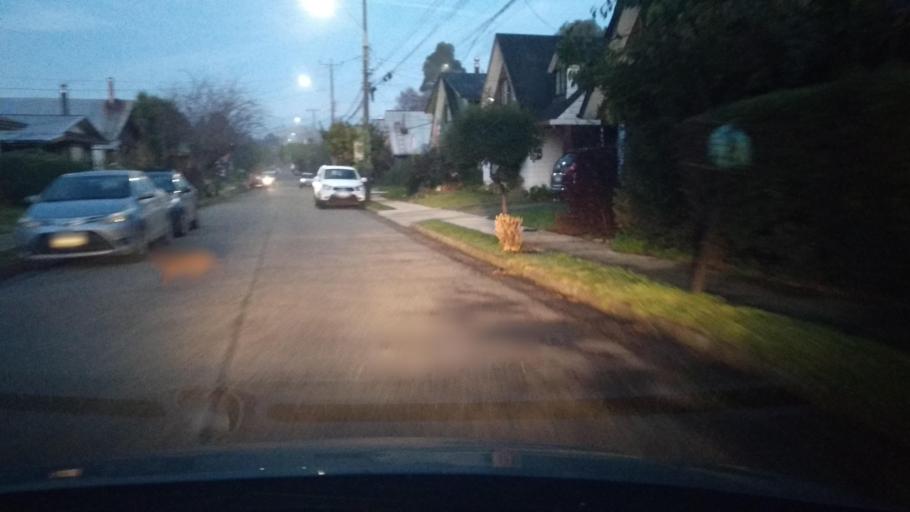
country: CL
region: Los Rios
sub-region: Provincia de Valdivia
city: Valdivia
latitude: -39.8105
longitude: -73.2620
